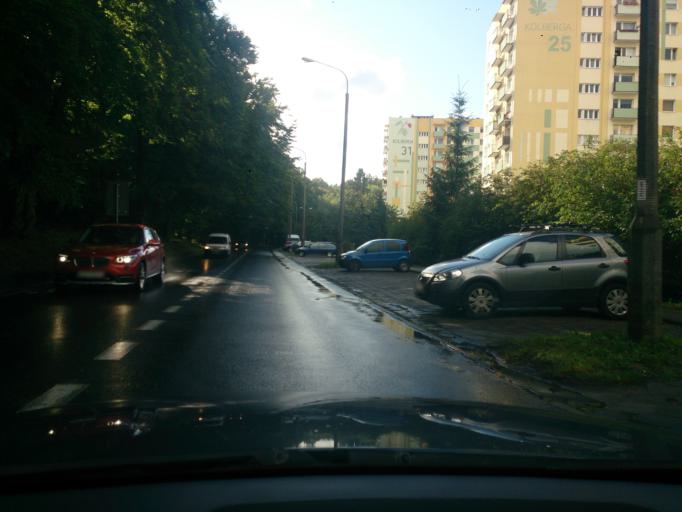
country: PL
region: Pomeranian Voivodeship
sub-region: Sopot
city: Sopot
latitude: 54.4559
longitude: 18.5304
